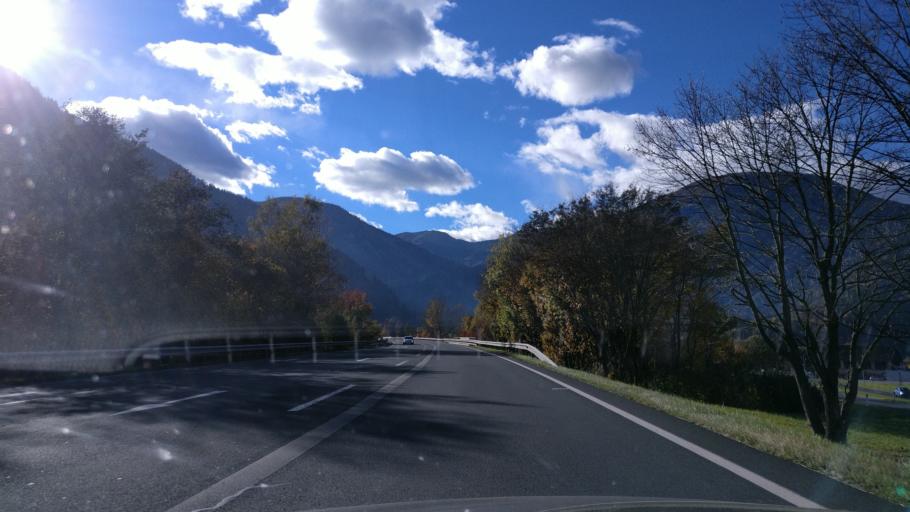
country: AT
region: Carinthia
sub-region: Politischer Bezirk Spittal an der Drau
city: Sachsenburg
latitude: 46.8322
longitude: 13.3849
